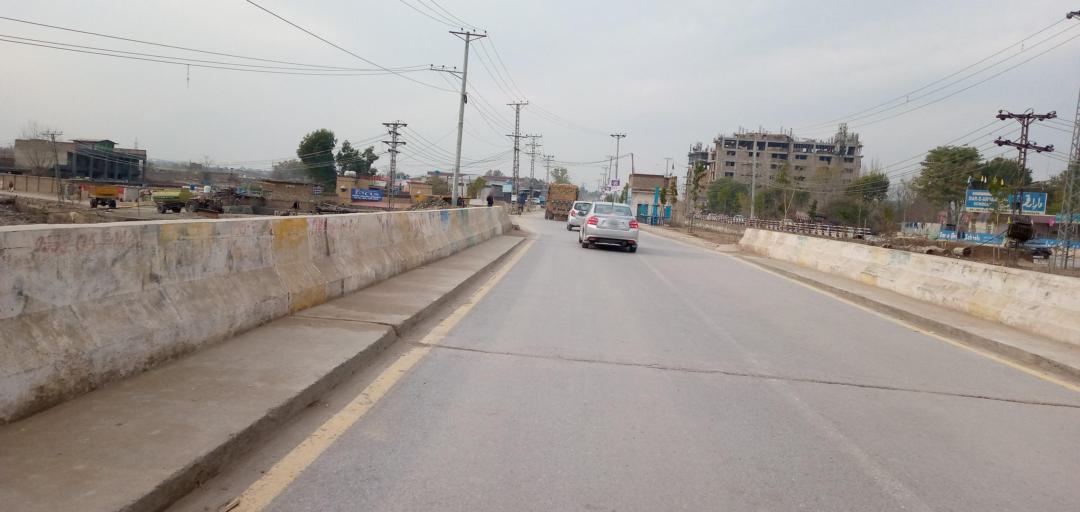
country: PK
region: Khyber Pakhtunkhwa
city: Peshawar
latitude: 34.0038
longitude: 71.4661
